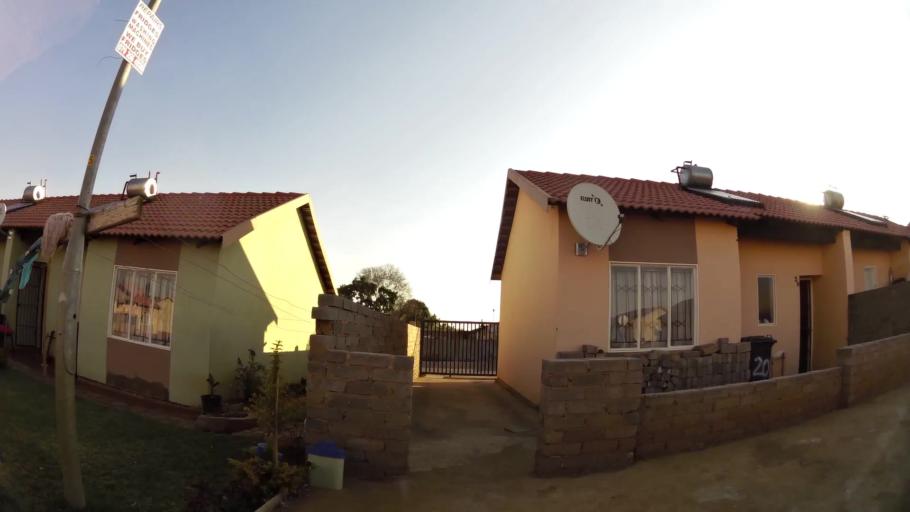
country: ZA
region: Gauteng
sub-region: City of Tshwane Metropolitan Municipality
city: Pretoria
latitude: -25.7411
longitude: 28.1205
